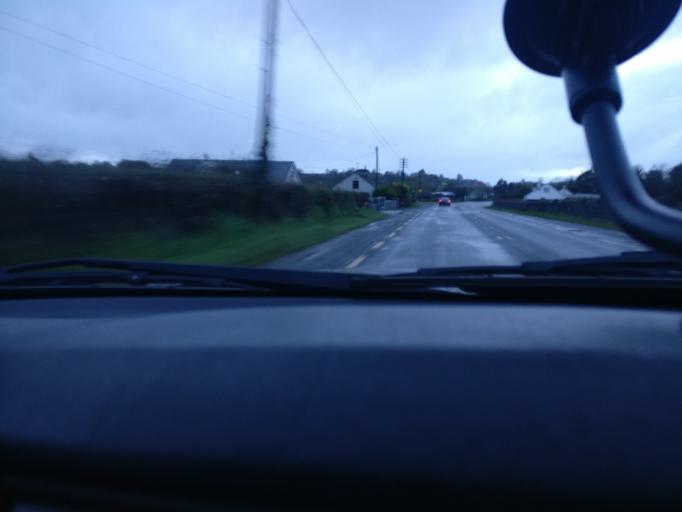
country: IE
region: Connaught
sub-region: County Galway
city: Ballinasloe
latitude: 53.3140
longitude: -8.2566
